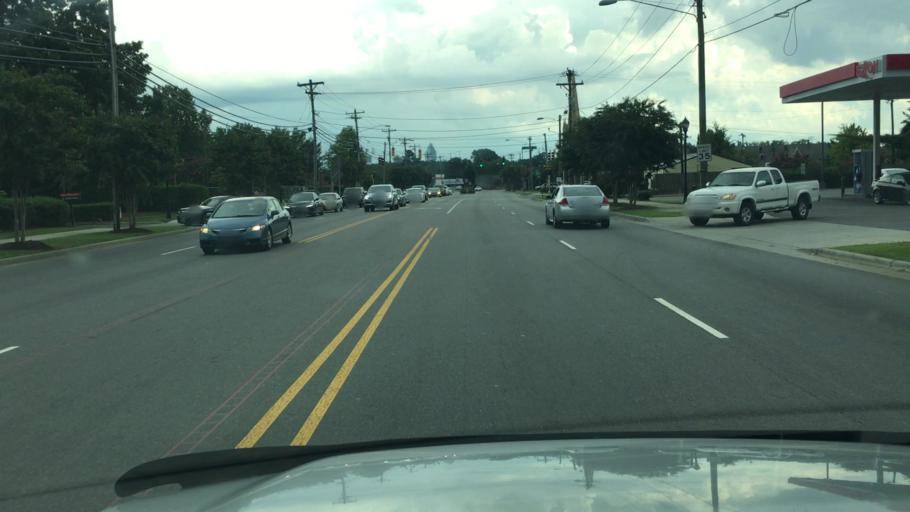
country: US
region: North Carolina
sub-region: Mecklenburg County
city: Charlotte
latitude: 35.2694
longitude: -80.8540
